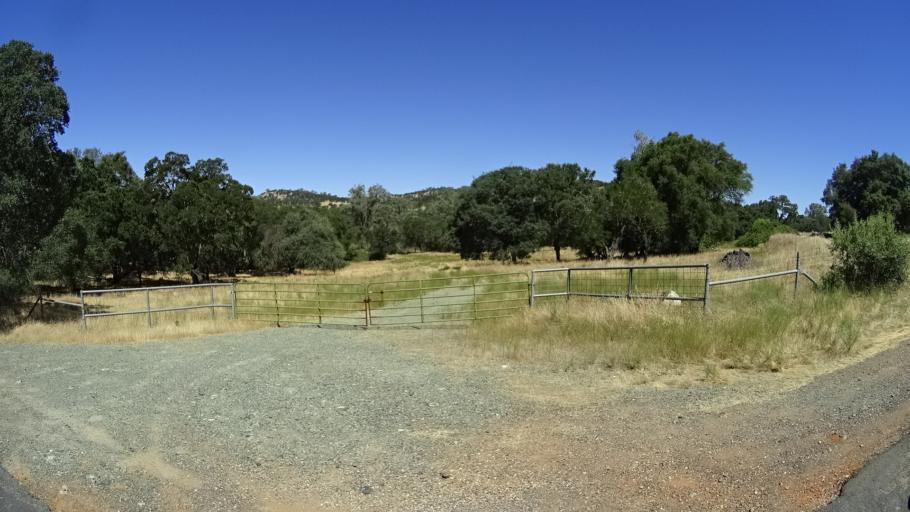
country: US
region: California
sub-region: Calaveras County
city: Copperopolis
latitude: 38.0234
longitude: -120.7640
